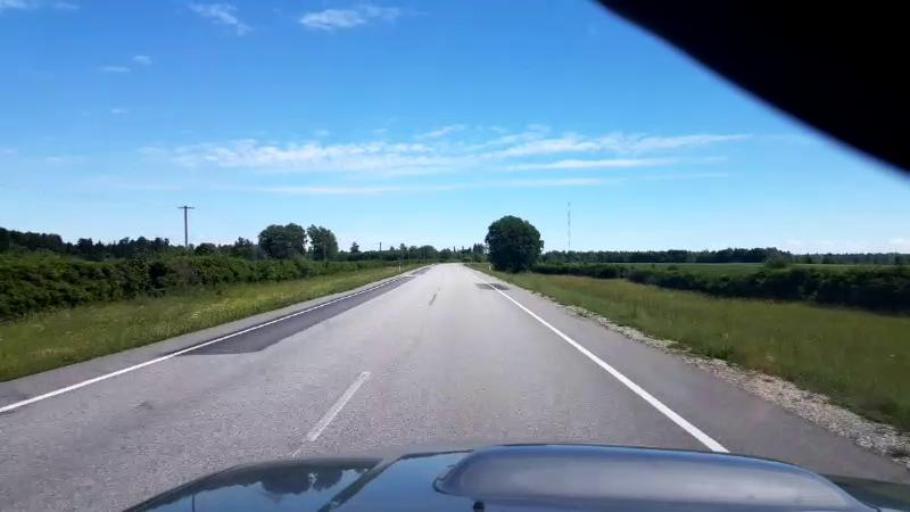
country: EE
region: Jaervamaa
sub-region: Koeru vald
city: Koeru
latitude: 58.9878
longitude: 25.9942
